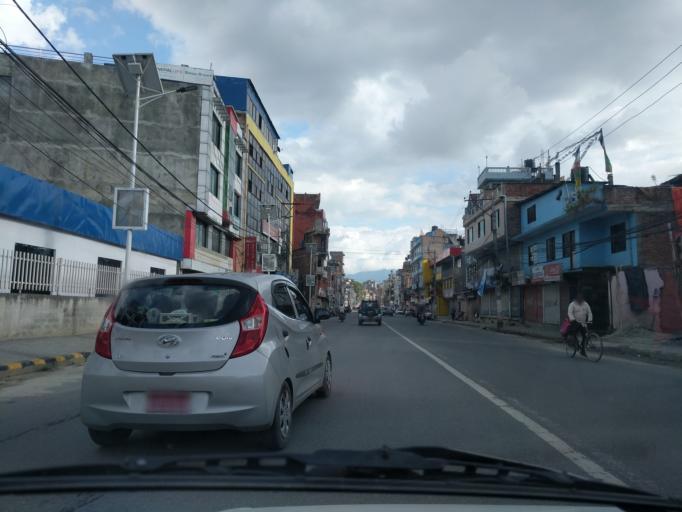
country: NP
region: Central Region
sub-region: Bagmati Zone
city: Kathmandu
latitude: 27.7243
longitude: 85.3063
